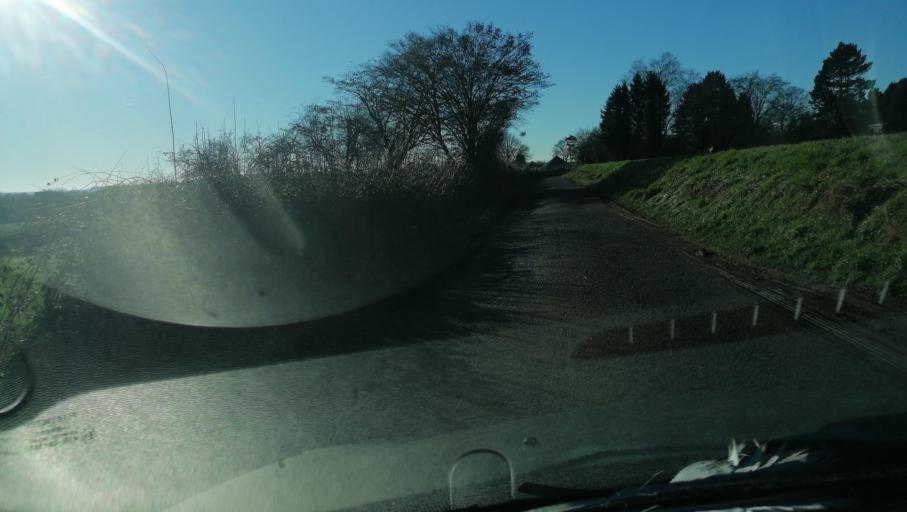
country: FR
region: Nord-Pas-de-Calais
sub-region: Departement du Nord
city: Ferriere-la-Grande
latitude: 50.2251
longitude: 4.0391
